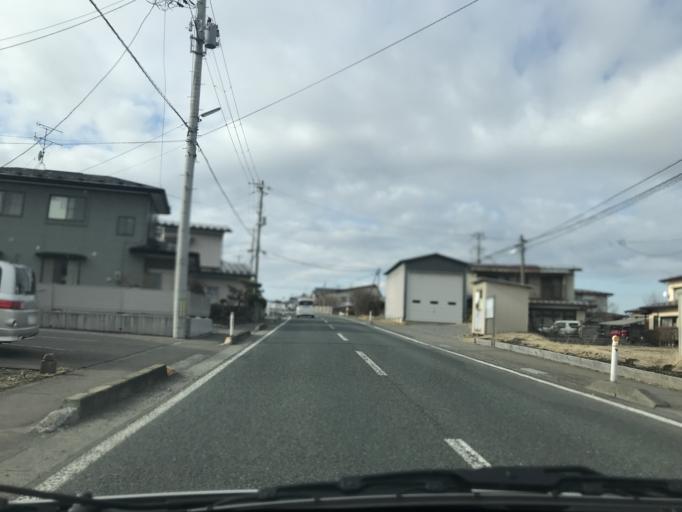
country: JP
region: Iwate
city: Hanamaki
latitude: 39.4049
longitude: 141.1148
